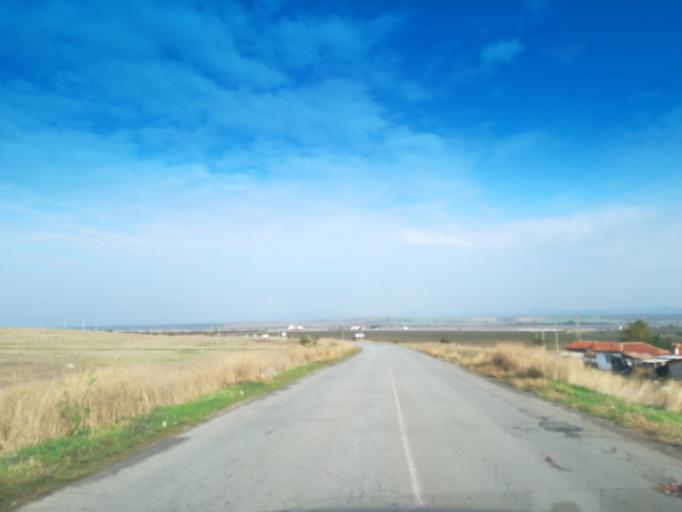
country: BG
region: Stara Zagora
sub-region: Obshtina Chirpan
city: Chirpan
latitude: 42.2033
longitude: 25.3089
